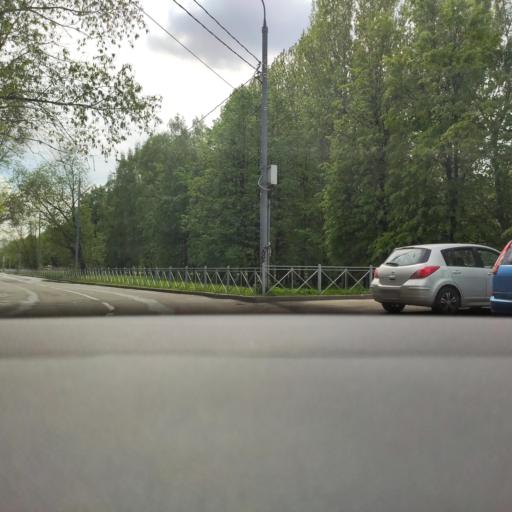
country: RU
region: Moscow
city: Vatutino
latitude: 55.8776
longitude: 37.6616
